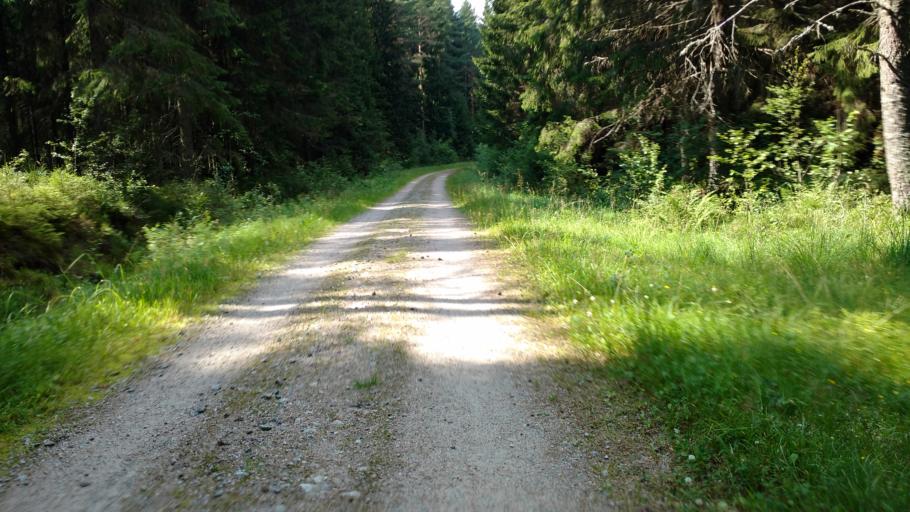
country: FI
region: Varsinais-Suomi
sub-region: Salo
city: Pertteli
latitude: 60.4007
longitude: 23.2168
